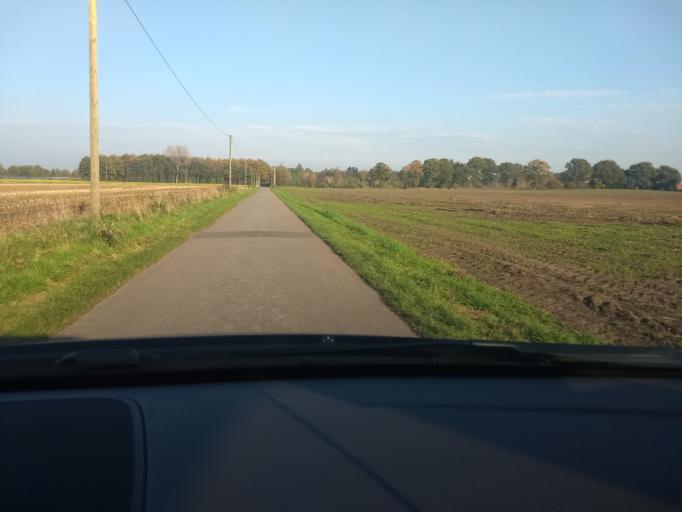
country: DE
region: North Rhine-Westphalia
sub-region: Regierungsbezirk Munster
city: Sudlohn
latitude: 51.9143
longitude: 6.8237
